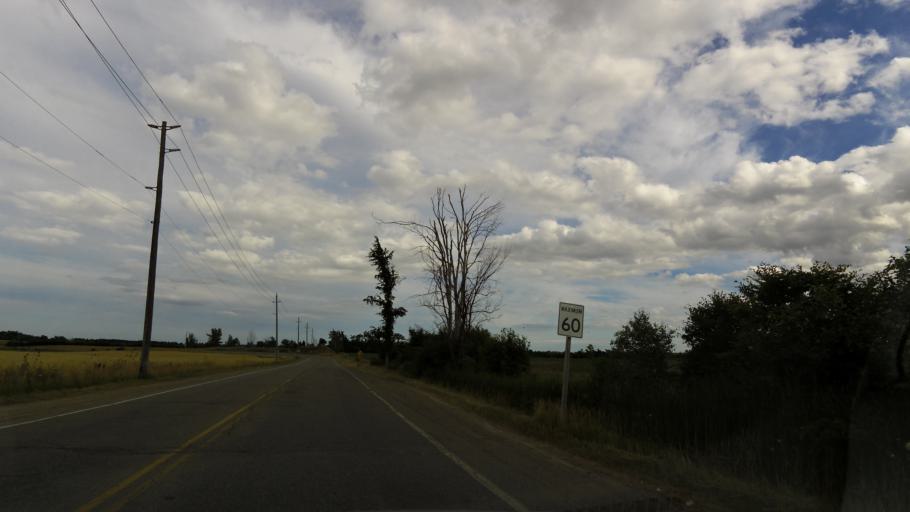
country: CA
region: Ontario
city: Brampton
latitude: 43.6670
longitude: -79.9020
